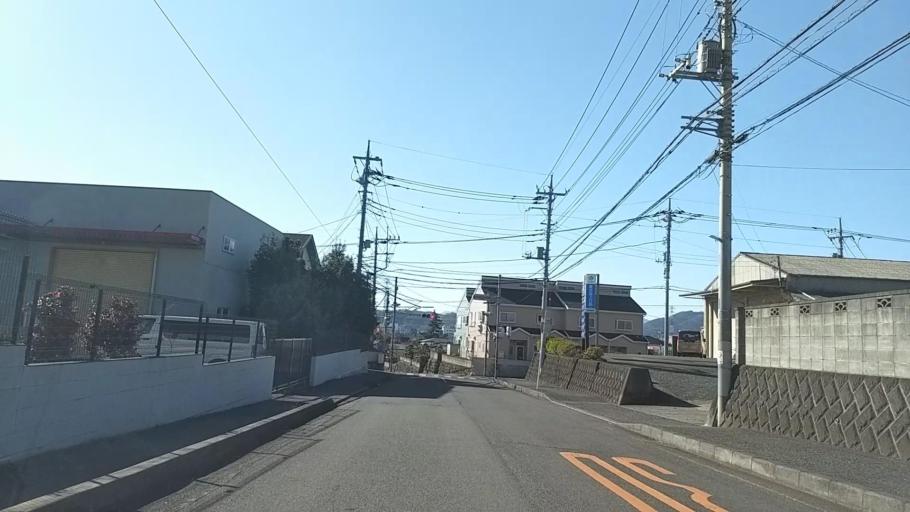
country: JP
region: Kanagawa
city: Hadano
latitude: 35.3883
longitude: 139.1993
